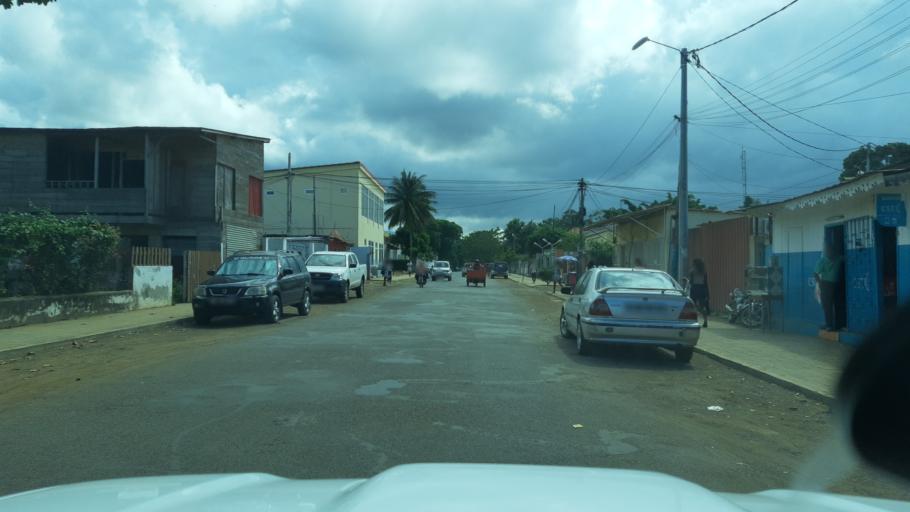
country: ST
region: Sao Tome Island
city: Sao Tome
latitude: 0.3368
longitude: 6.7351
